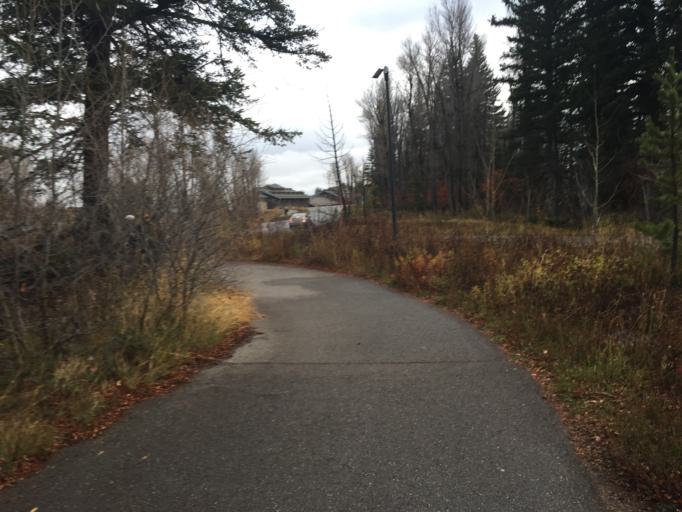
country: US
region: Wyoming
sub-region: Teton County
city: Jackson
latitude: 43.6537
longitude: -110.7178
